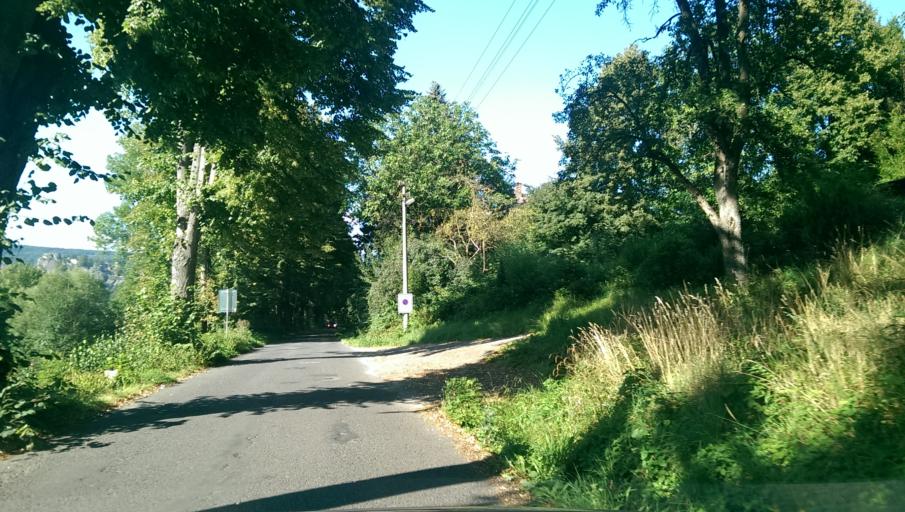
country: CZ
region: Liberecky
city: Mala Skala
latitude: 50.6318
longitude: 15.1921
